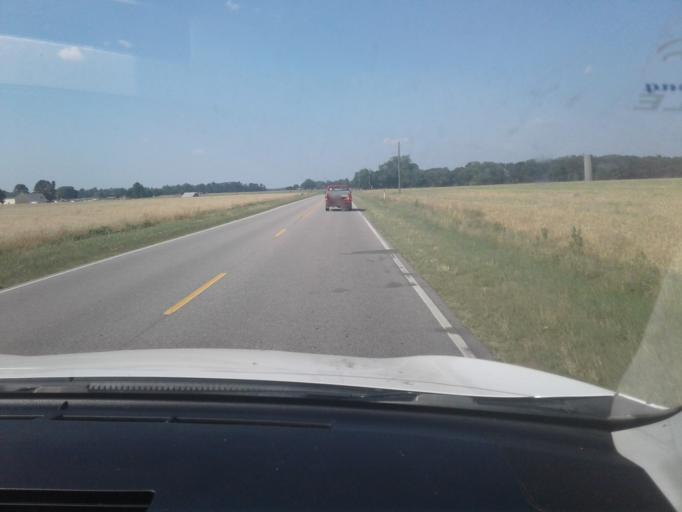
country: US
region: North Carolina
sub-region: Harnett County
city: Coats
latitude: 35.3664
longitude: -78.6328
